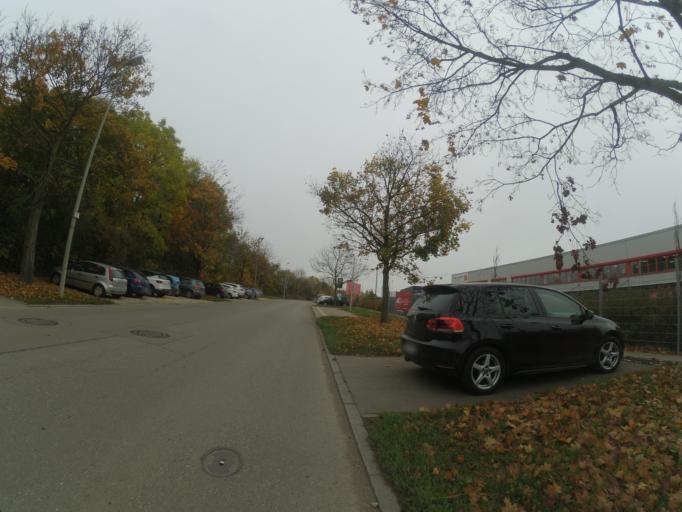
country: DE
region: Baden-Wuerttemberg
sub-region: Tuebingen Region
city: Erbach
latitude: 48.3540
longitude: 9.9260
